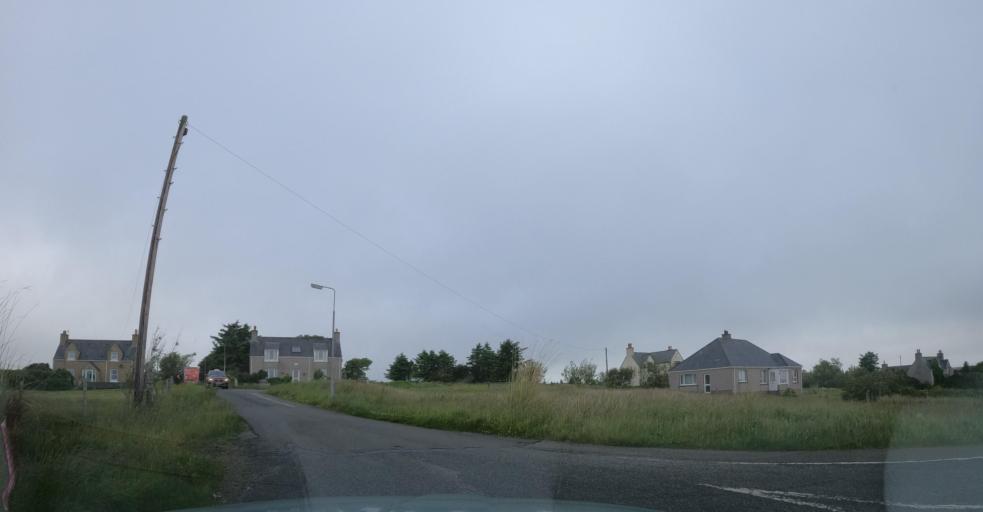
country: GB
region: Scotland
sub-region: Eilean Siar
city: Stornoway
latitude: 58.2003
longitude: -6.2247
